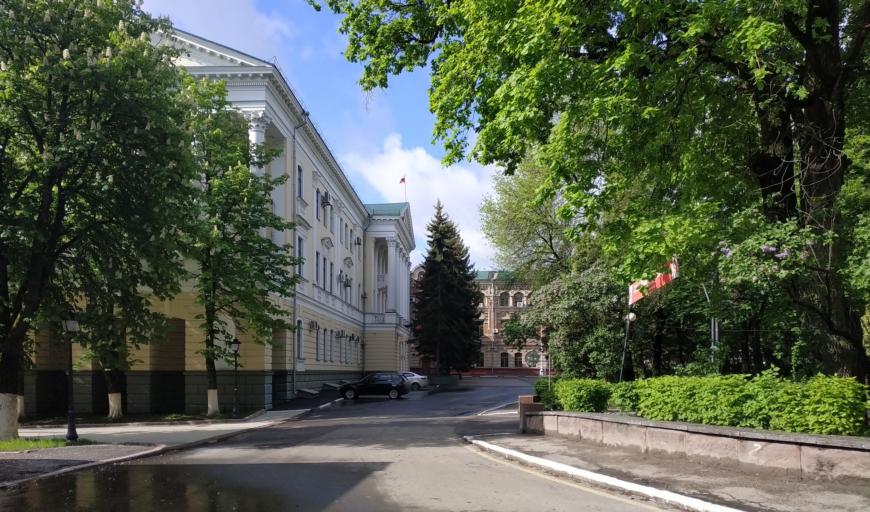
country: RU
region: Brjansk
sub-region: Bryanskiy Rayon
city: Bryansk
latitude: 53.2422
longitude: 34.3673
